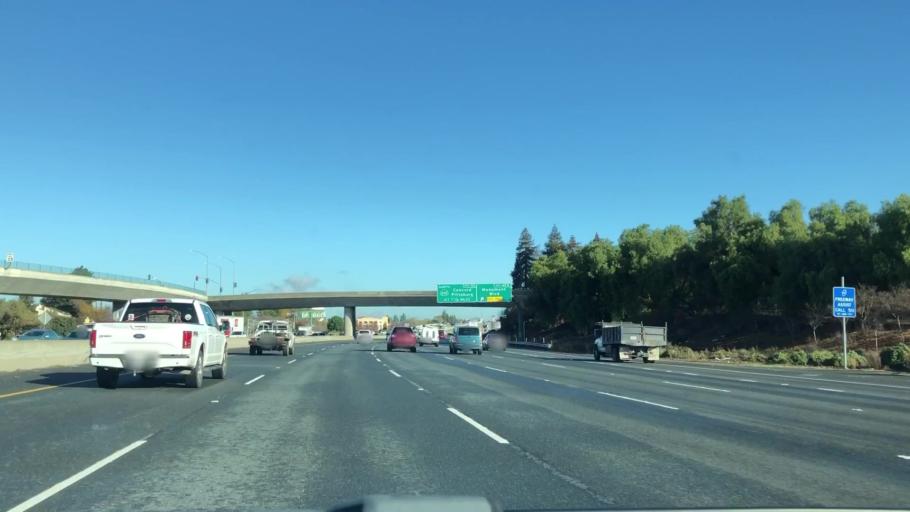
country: US
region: California
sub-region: Contra Costa County
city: Pleasant Hill
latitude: 37.9395
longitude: -122.0602
